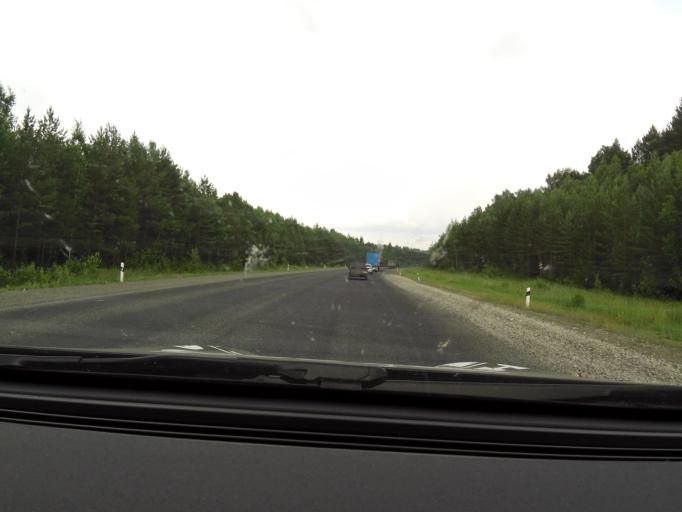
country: RU
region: Sverdlovsk
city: Ufimskiy
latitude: 56.7658
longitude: 58.1672
